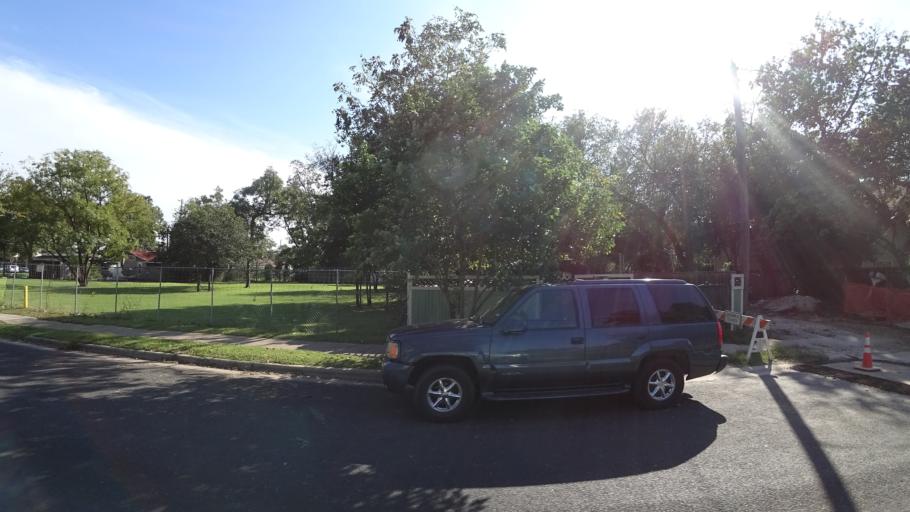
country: US
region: Texas
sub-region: Travis County
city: Austin
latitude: 30.2606
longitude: -97.7284
